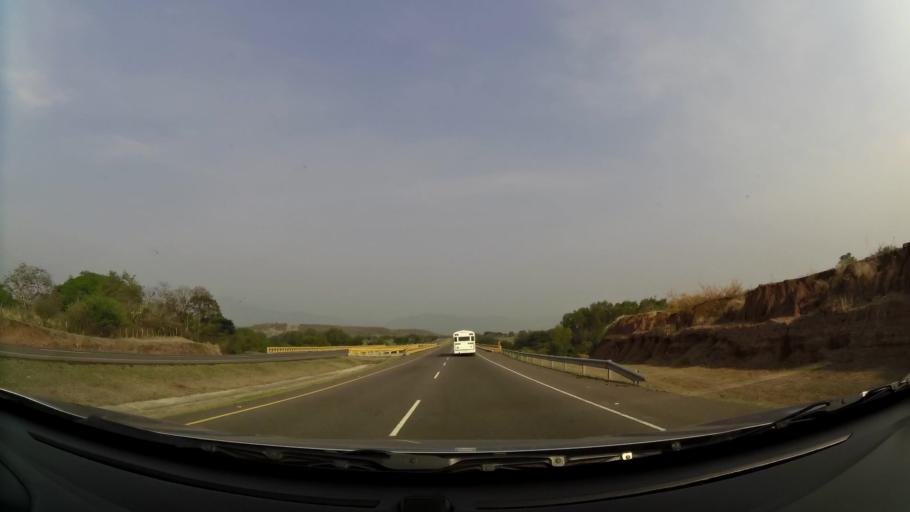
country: HN
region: Comayagua
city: Comayagua
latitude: 14.4326
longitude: -87.6485
